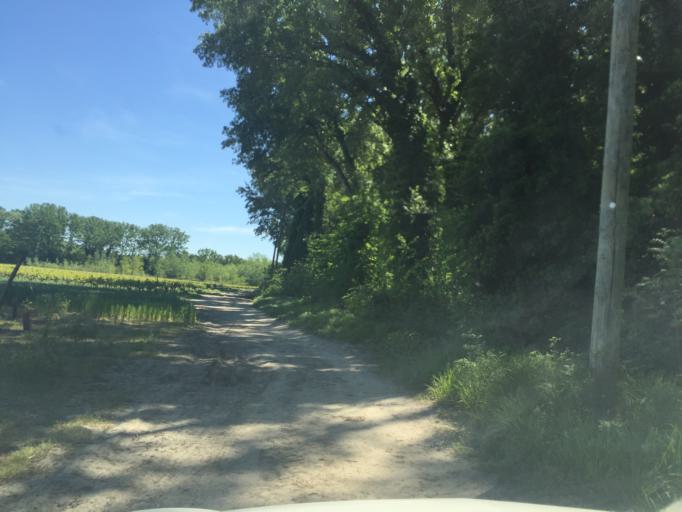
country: FR
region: Languedoc-Roussillon
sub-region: Departement du Gard
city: Roquemaure
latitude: 44.0515
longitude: 4.7987
